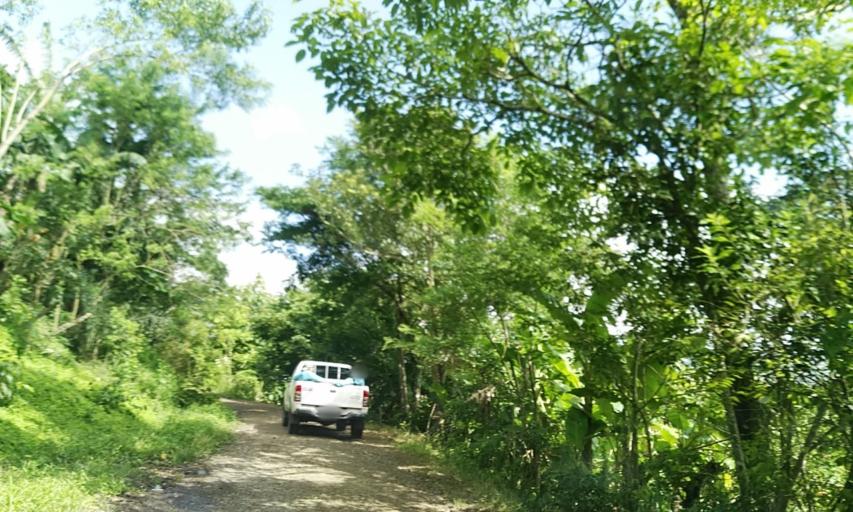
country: NI
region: Matagalpa
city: San Ramon
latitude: 12.9923
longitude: -85.8622
